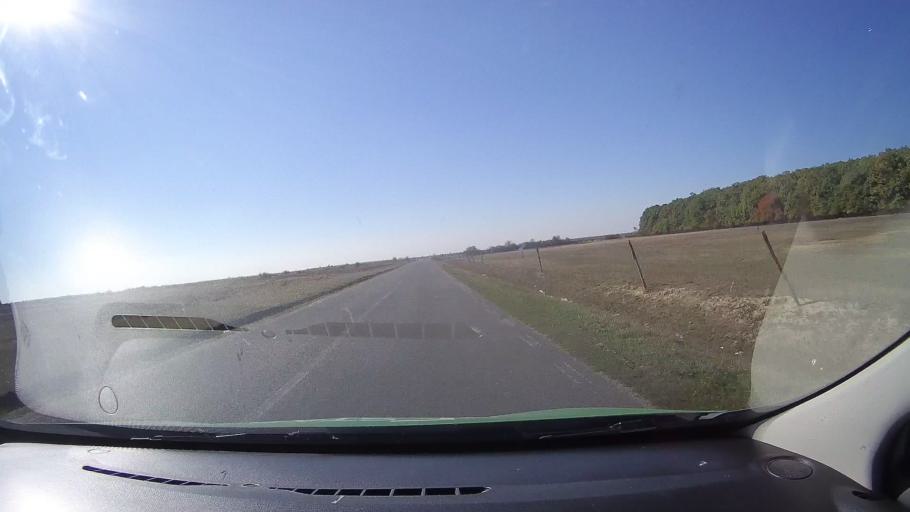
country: RO
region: Satu Mare
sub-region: Municipiul Satu Mare
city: Satmarel
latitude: 47.7014
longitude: 22.7732
